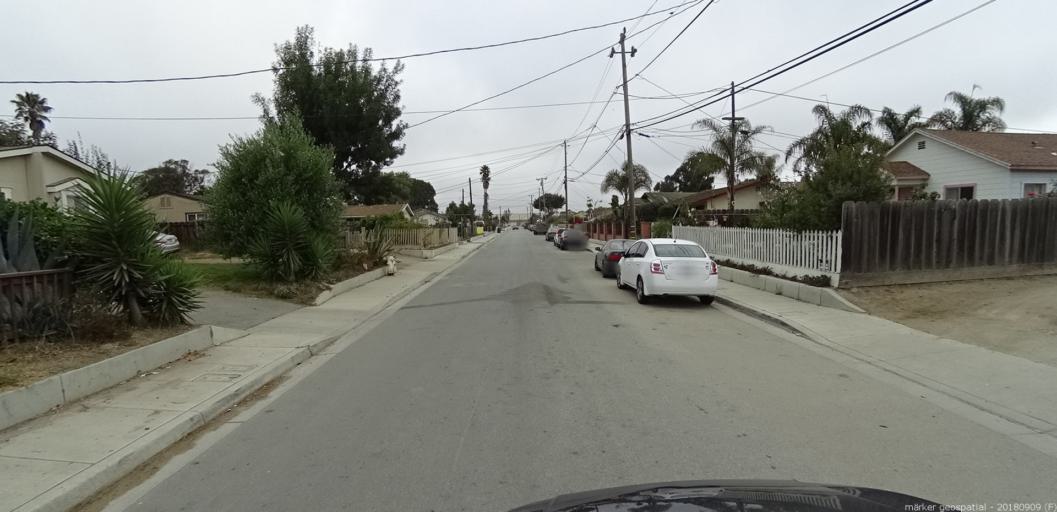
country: US
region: California
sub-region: Monterey County
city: Boronda
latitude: 36.7002
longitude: -121.6711
